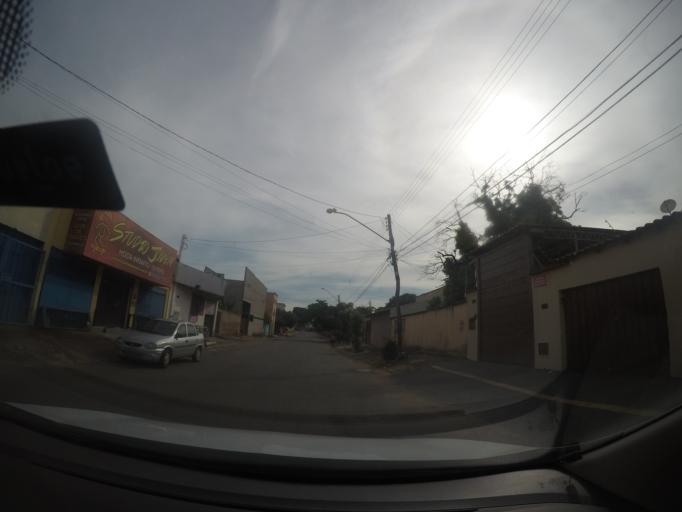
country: BR
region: Goias
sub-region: Goiania
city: Goiania
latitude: -16.6592
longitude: -49.3071
